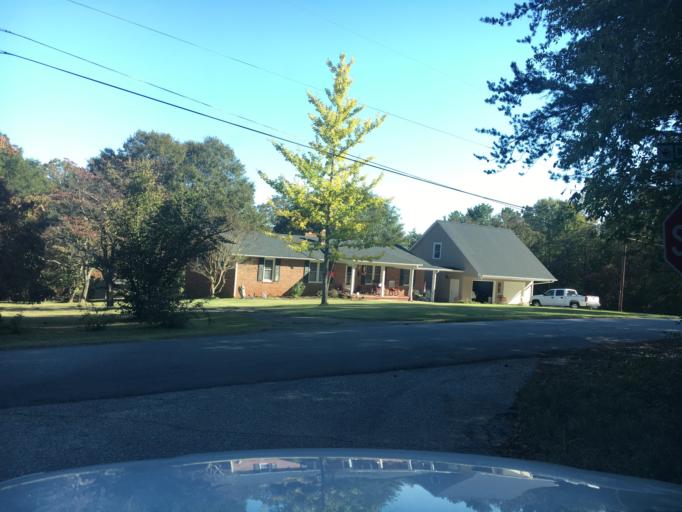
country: US
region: South Carolina
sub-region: Spartanburg County
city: Lyman
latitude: 34.9142
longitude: -82.1173
